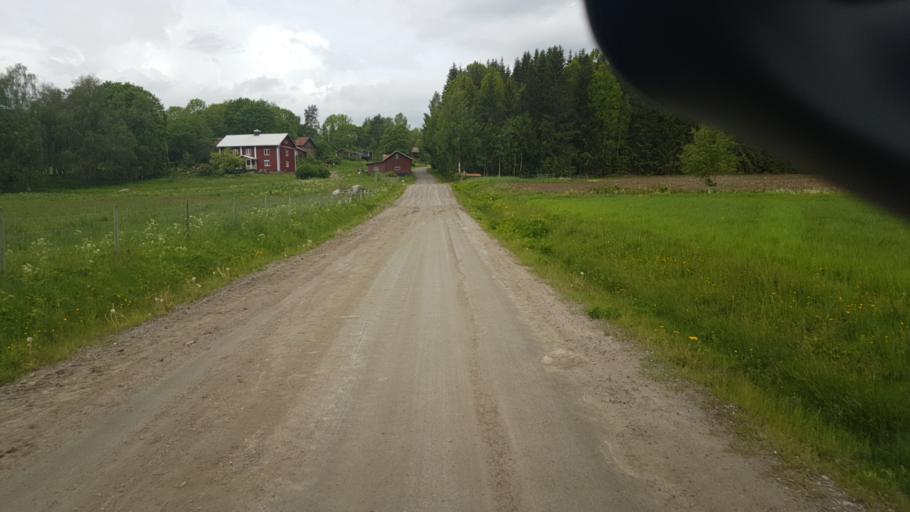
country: SE
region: Vaermland
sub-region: Arvika Kommun
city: Arvika
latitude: 59.8323
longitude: 12.5411
